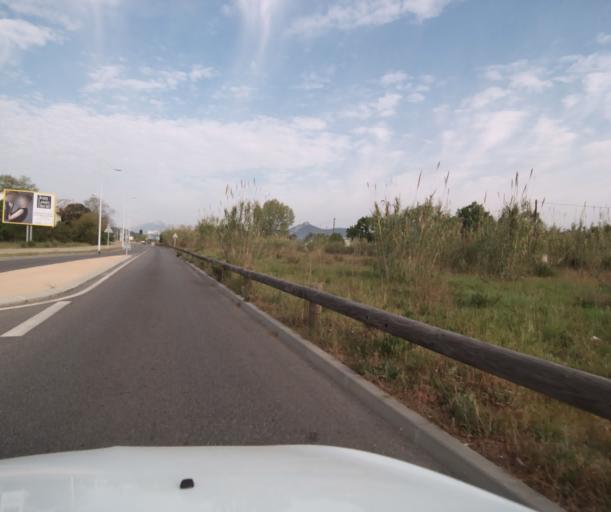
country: FR
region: Provence-Alpes-Cote d'Azur
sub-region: Departement du Var
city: Hyeres
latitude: 43.1119
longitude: 6.1211
